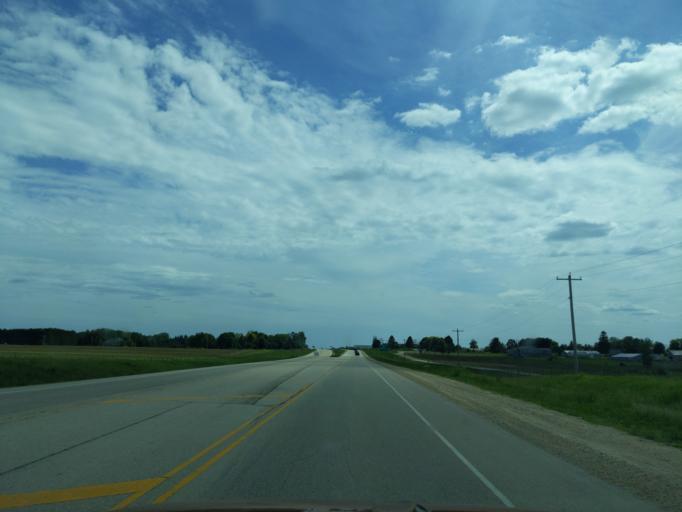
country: US
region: Wisconsin
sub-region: Dane County
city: De Forest
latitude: 43.2719
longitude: -89.3247
